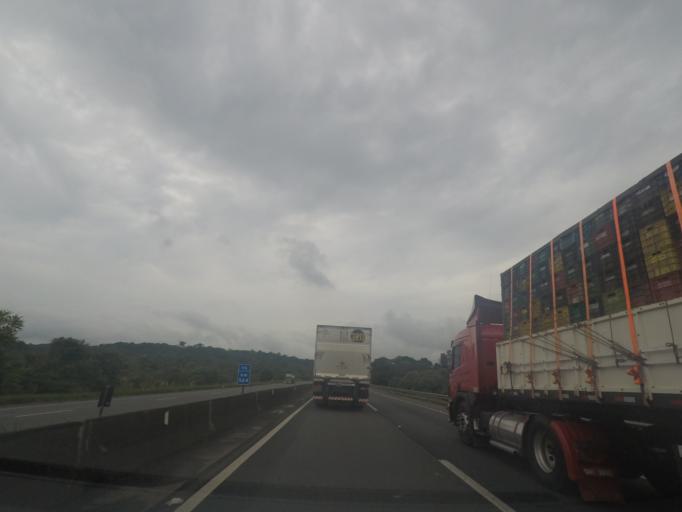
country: BR
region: Sao Paulo
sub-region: Cajati
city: Cajati
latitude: -24.9194
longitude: -48.2585
